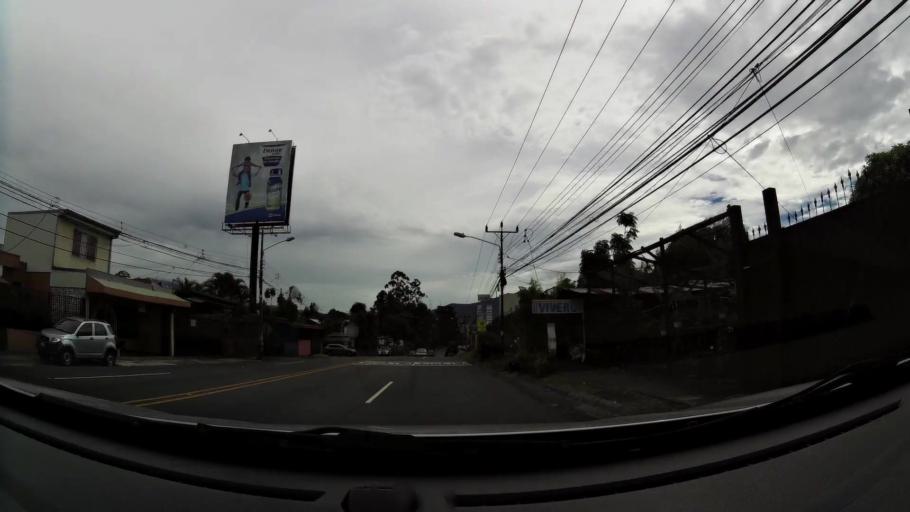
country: CR
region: San Jose
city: Curridabat
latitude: 9.9174
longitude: -84.0428
